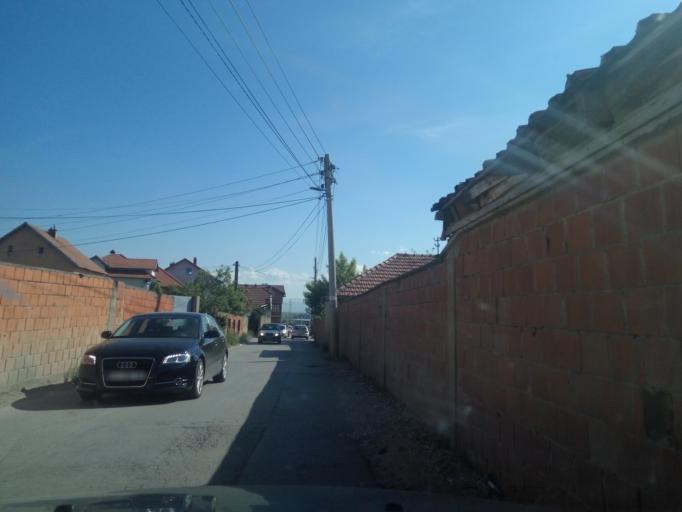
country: XK
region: Pristina
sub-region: Kosovo Polje
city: Kosovo Polje
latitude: 42.6554
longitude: 21.1275
